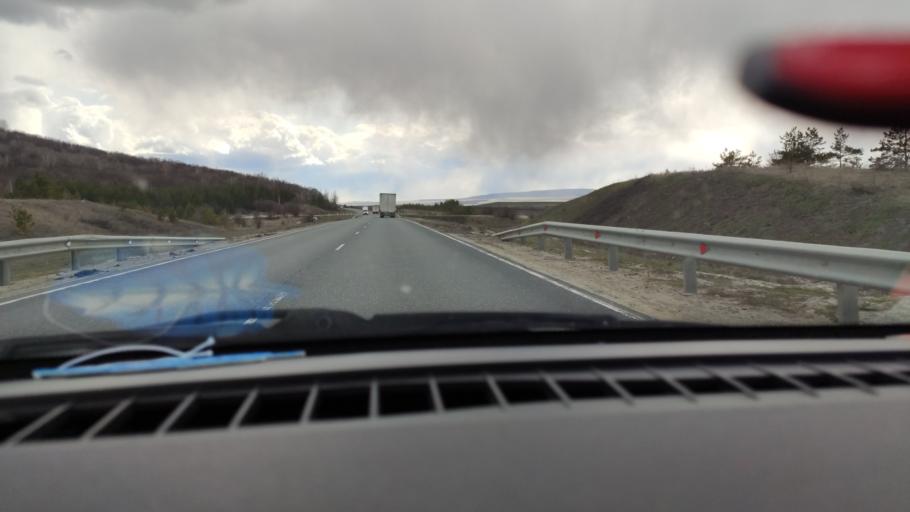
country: RU
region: Saratov
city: Alekseyevka
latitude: 52.3934
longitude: 47.9796
